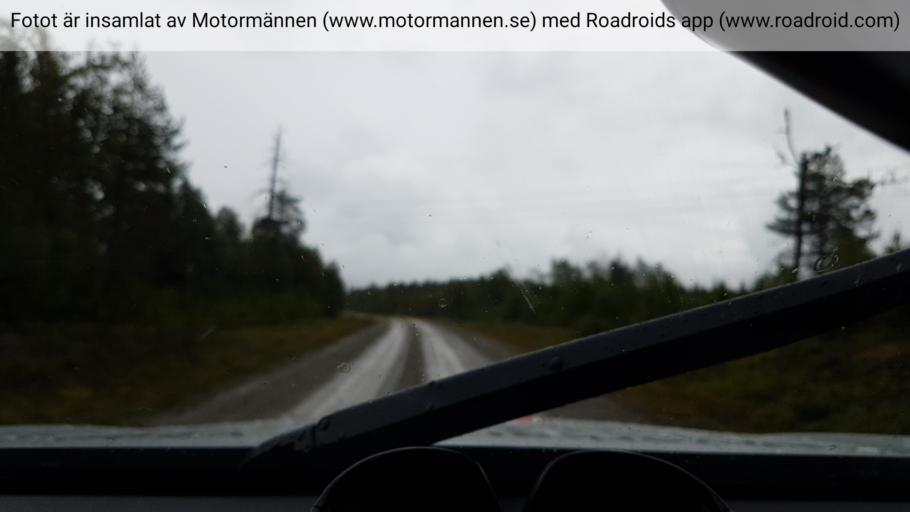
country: SE
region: Vaesterbotten
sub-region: Asele Kommun
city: Insjon
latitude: 64.7844
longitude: 17.5743
